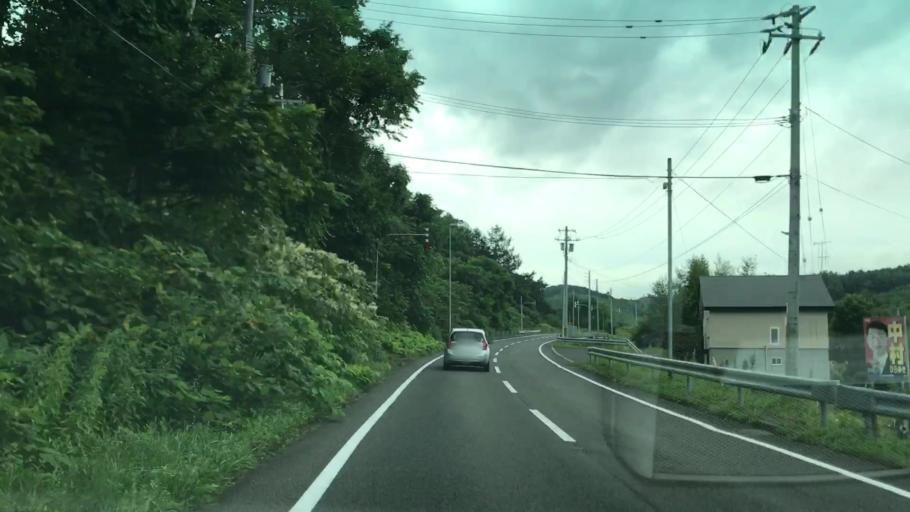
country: JP
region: Hokkaido
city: Yoichi
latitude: 43.1512
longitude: 140.8221
